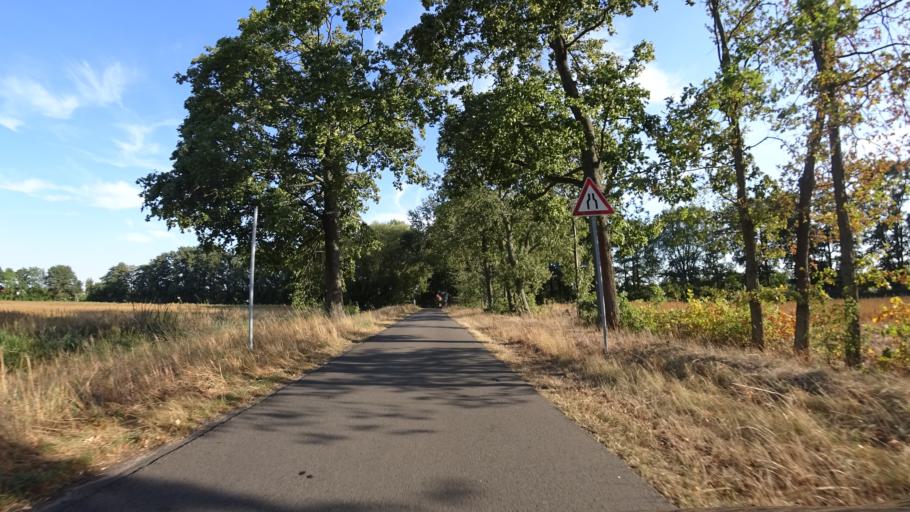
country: DE
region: Brandenburg
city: Stahnsdorf
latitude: 52.3310
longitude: 13.1645
